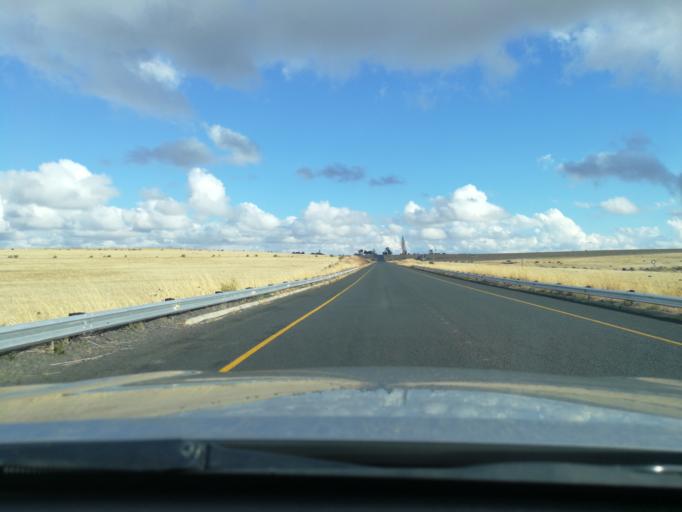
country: ZA
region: Orange Free State
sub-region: Thabo Mofutsanyana District Municipality
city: Reitz
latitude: -27.9069
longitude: 28.3954
